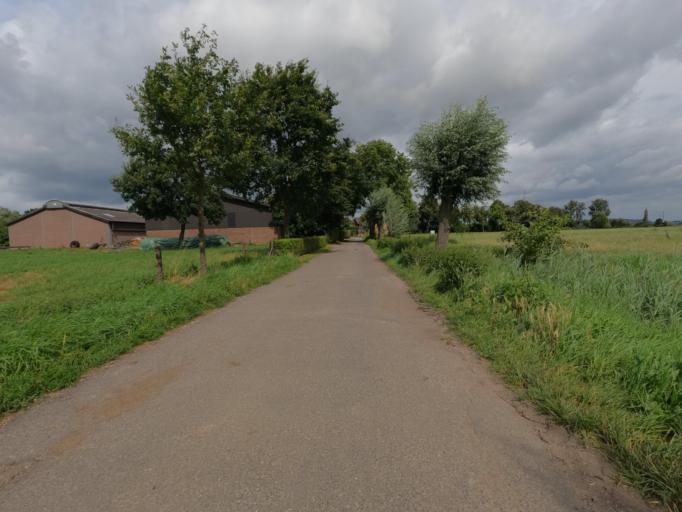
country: DE
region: North Rhine-Westphalia
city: Huckelhoven
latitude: 51.0266
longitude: 6.1805
